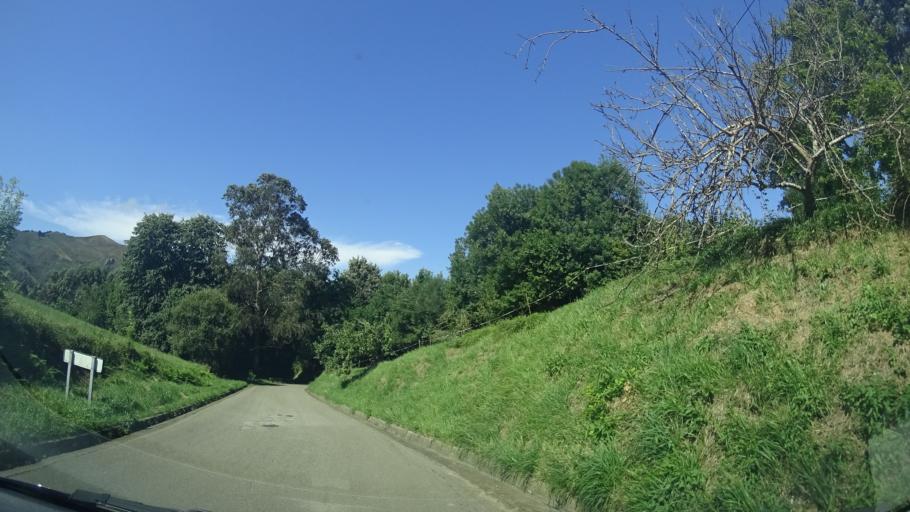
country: ES
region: Asturias
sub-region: Province of Asturias
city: Ribadesella
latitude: 43.4432
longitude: -5.0882
